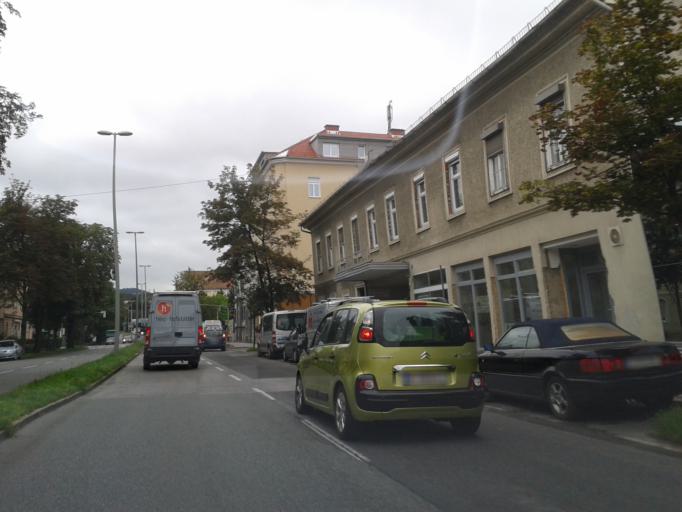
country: AT
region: Styria
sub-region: Graz Stadt
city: Goesting
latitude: 47.0854
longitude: 15.4193
